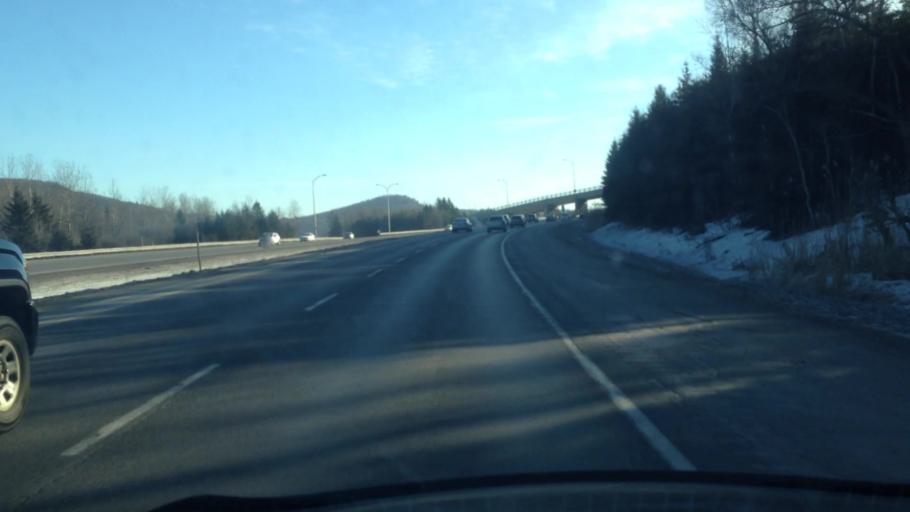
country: CA
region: Quebec
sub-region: Laurentides
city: Prevost
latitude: 45.8847
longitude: -74.1094
